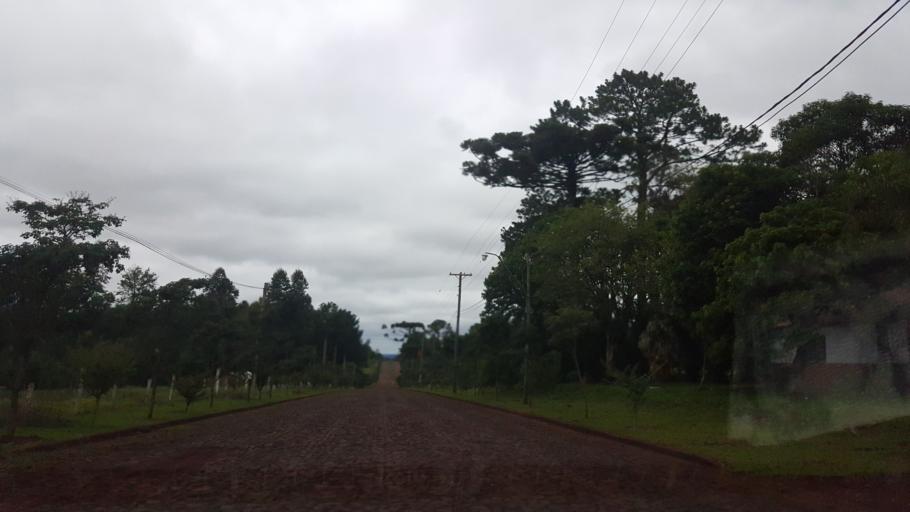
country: AR
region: Misiones
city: Ruiz de Montoya
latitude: -26.9595
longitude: -55.0562
